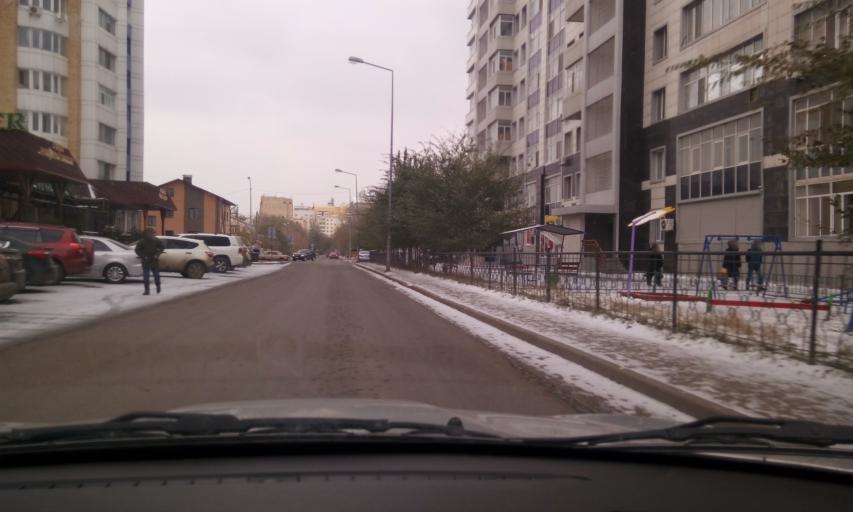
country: KZ
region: Astana Qalasy
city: Astana
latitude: 51.1623
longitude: 71.4324
